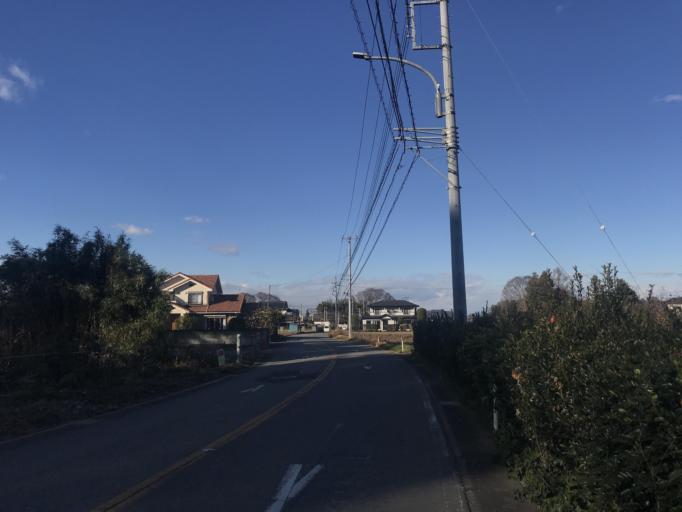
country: JP
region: Tochigi
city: Kaminokawa
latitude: 36.4172
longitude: 139.8776
